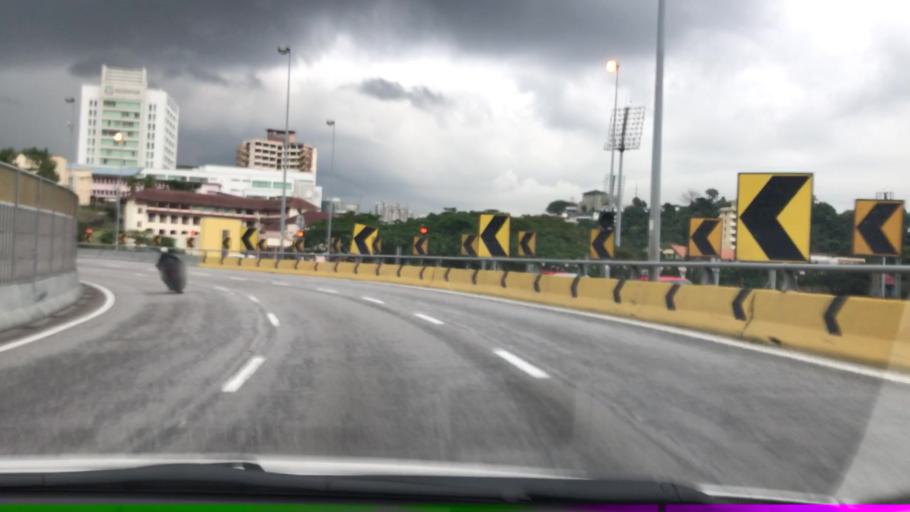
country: MY
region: Kuala Lumpur
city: Kuala Lumpur
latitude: 3.1182
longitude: 101.6635
